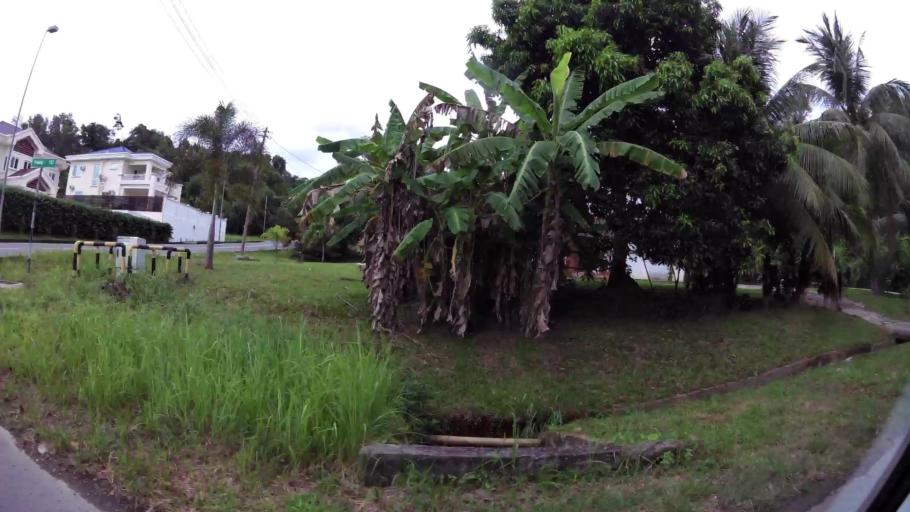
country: BN
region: Brunei and Muara
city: Bandar Seri Begawan
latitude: 4.8891
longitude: 114.9067
